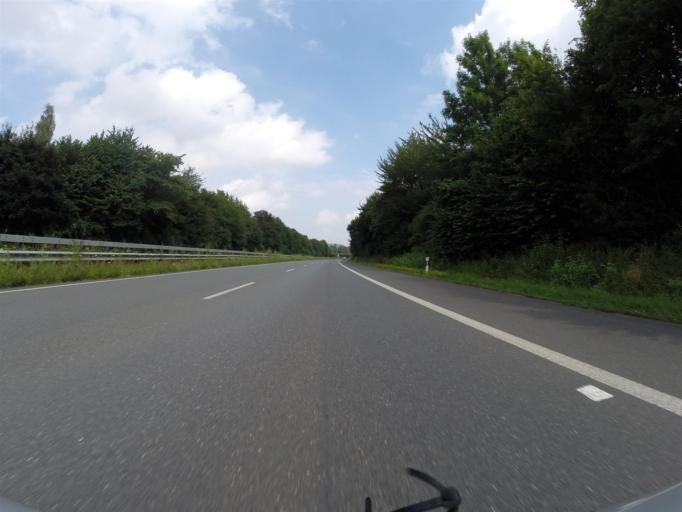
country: DE
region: North Rhine-Westphalia
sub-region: Regierungsbezirk Detmold
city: Herford
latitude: 52.1232
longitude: 8.6428
